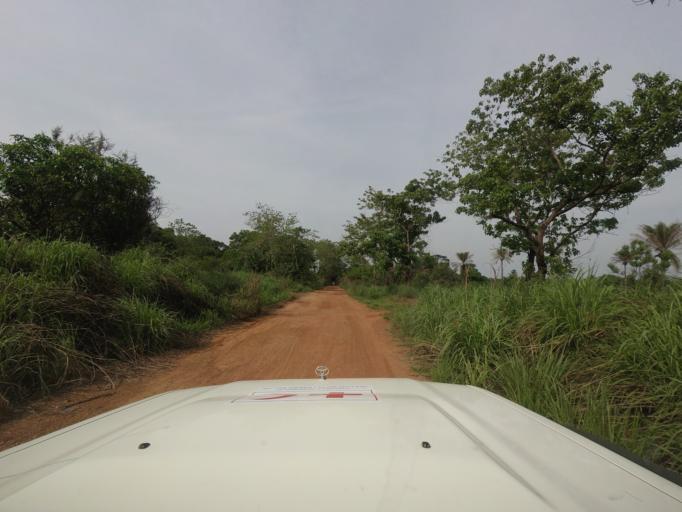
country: GN
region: Nzerekore
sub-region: Macenta
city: Macenta
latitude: 8.5324
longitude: -9.5031
